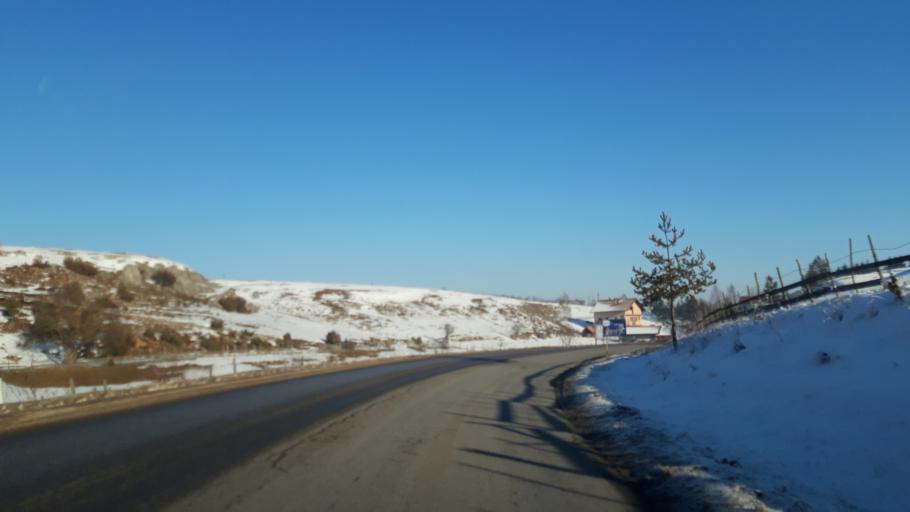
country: BA
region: Republika Srpska
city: Sokolac
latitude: 43.9183
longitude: 18.7624
